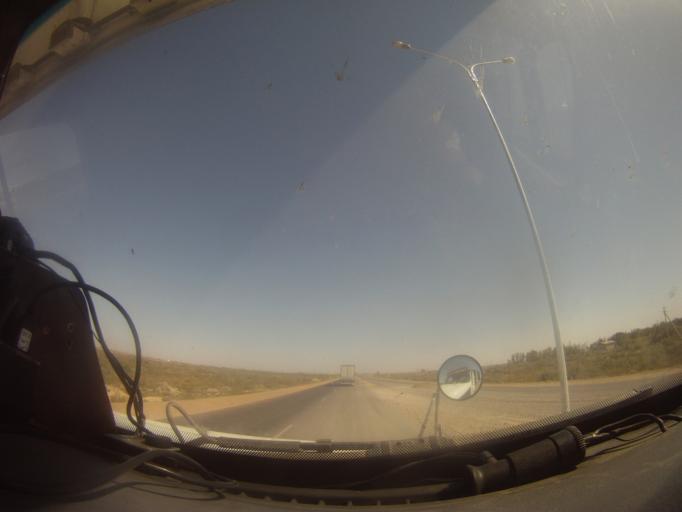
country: KZ
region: Qyzylorda
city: Tasboget
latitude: 44.7659
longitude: 65.5040
